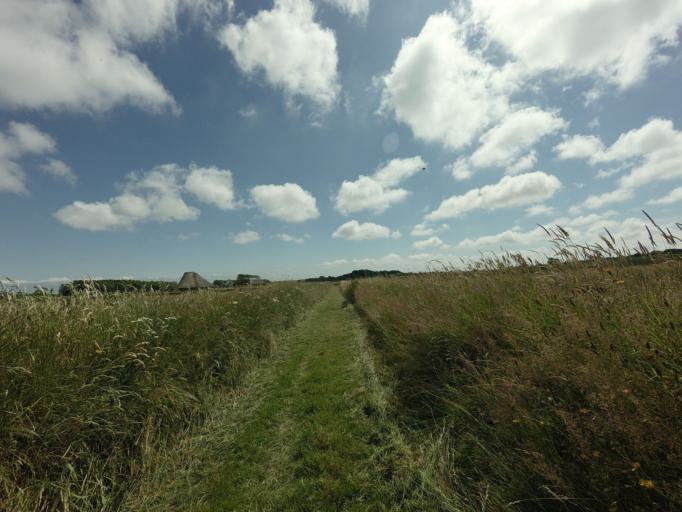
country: NL
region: North Holland
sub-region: Gemeente Texel
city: Den Burg
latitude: 53.0393
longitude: 4.8167
